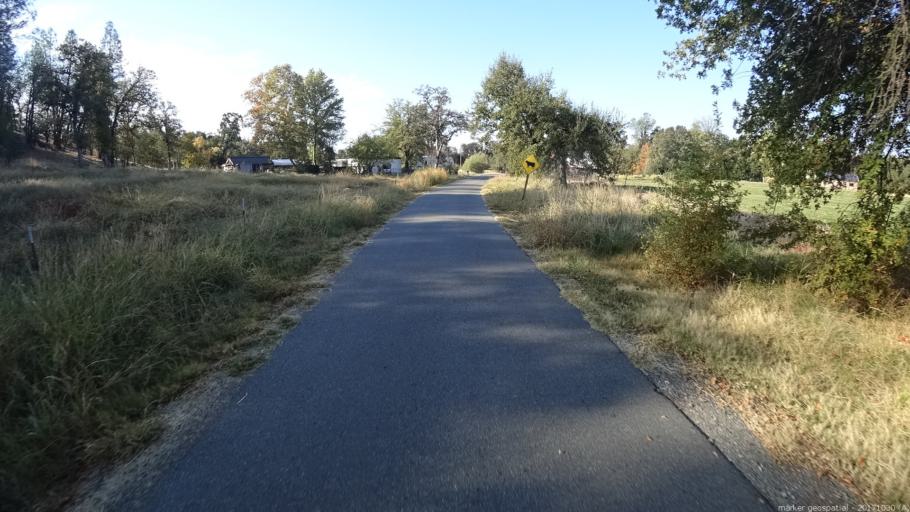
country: US
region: California
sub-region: Shasta County
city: Palo Cedro
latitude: 40.5623
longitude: -122.1562
